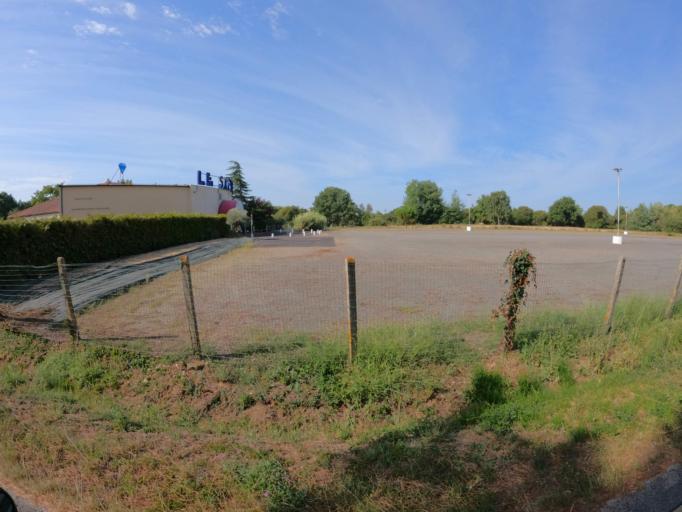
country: FR
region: Pays de la Loire
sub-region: Departement de la Vendee
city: Saint-Christophe-du-Ligneron
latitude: 46.8126
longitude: -1.8111
